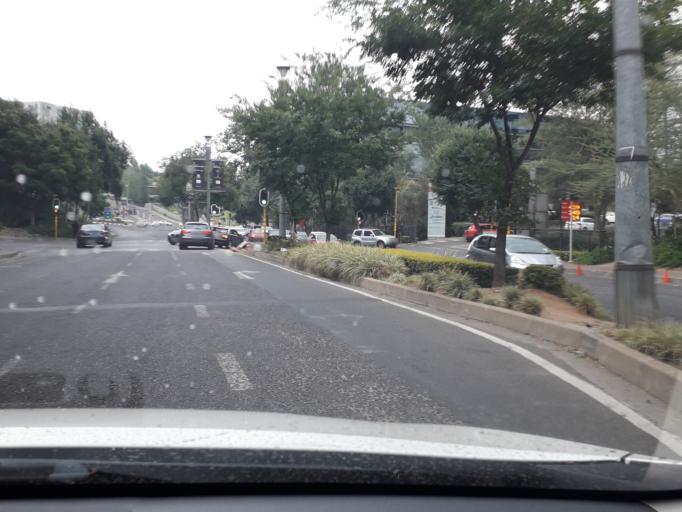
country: ZA
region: Gauteng
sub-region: City of Johannesburg Metropolitan Municipality
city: Johannesburg
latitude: -26.1092
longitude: 28.0513
